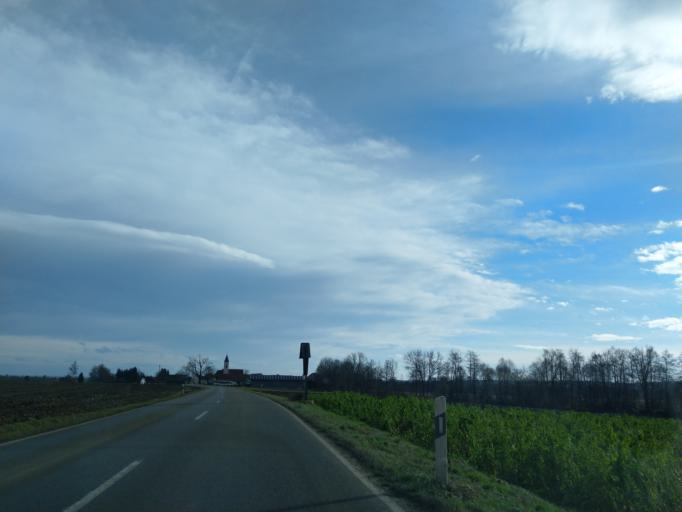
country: DE
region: Bavaria
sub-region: Lower Bavaria
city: Rossbach
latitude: 48.6298
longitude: 12.9490
